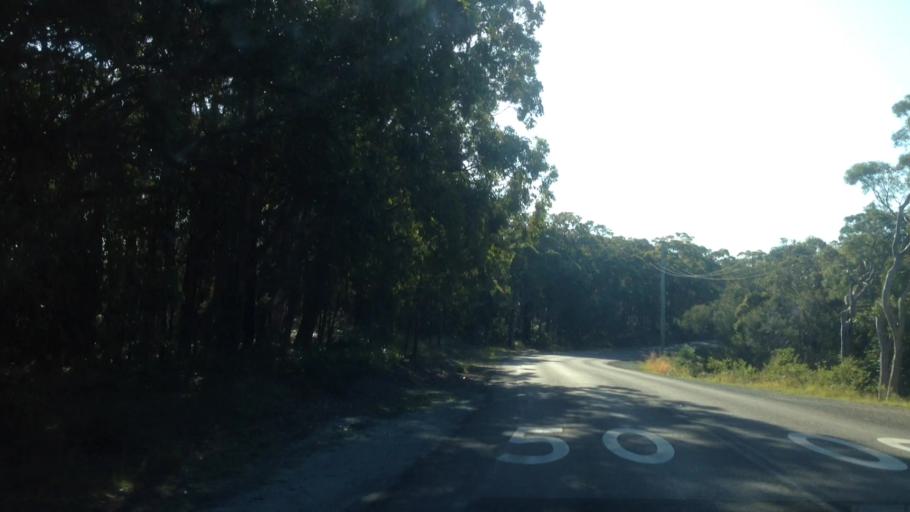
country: AU
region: New South Wales
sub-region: Lake Macquarie Shire
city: Arcadia vale
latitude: -33.1104
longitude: 151.5602
